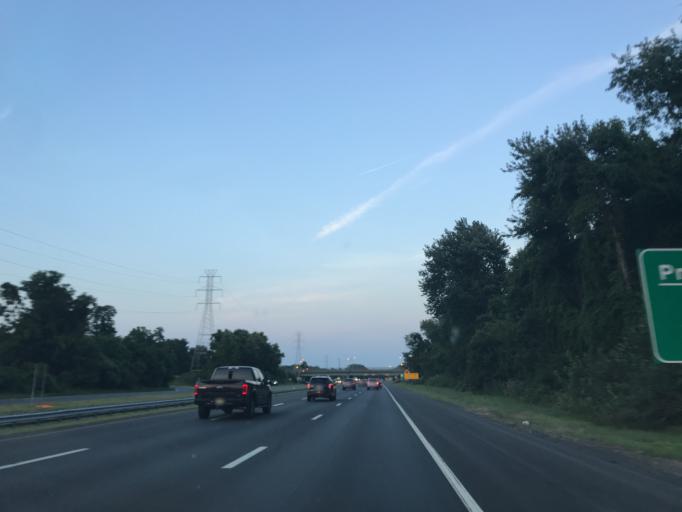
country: US
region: New Jersey
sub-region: Mercer County
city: Lawrenceville
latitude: 40.2856
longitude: -74.7172
